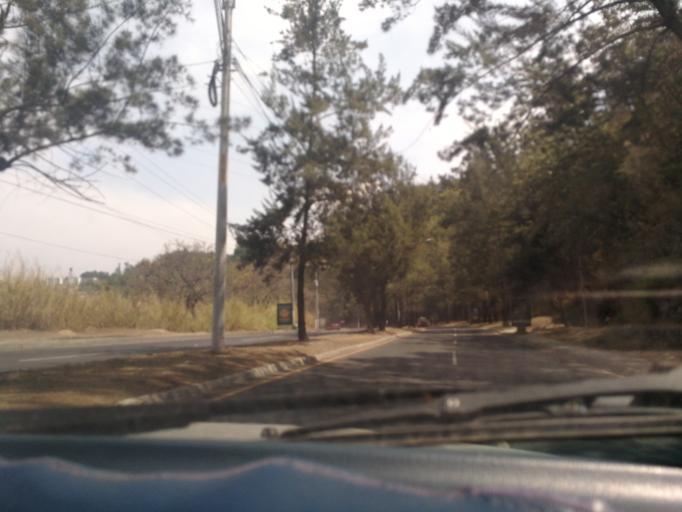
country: GT
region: Guatemala
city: Guatemala City
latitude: 14.6267
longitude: -90.4829
